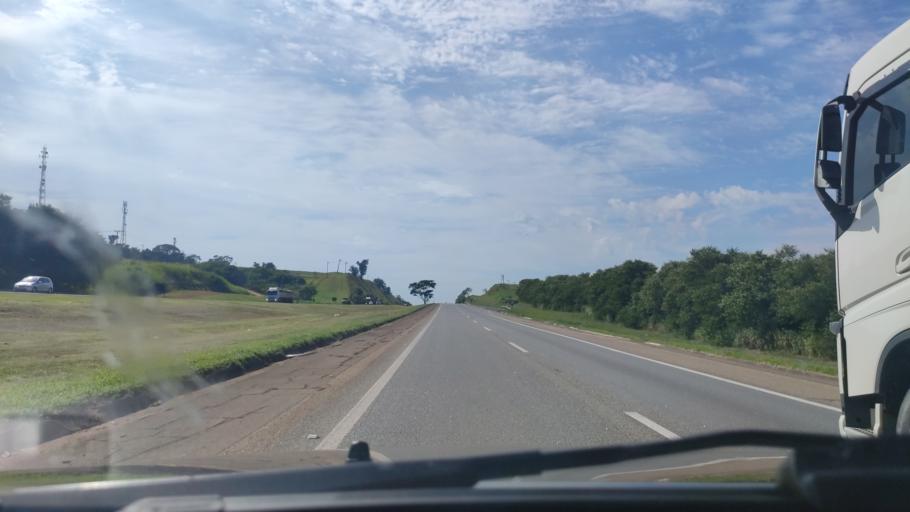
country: BR
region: Sao Paulo
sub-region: Boituva
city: Boituva
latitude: -23.3193
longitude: -47.6051
